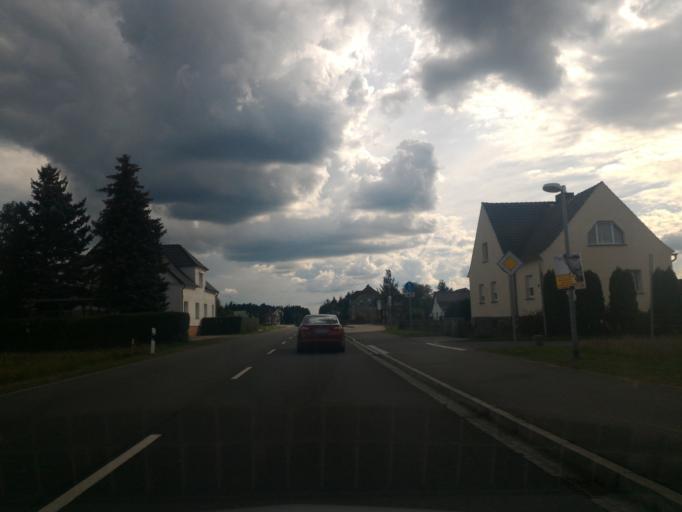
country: DE
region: Saxony
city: Weisskeissel
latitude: 51.4898
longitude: 14.7226
